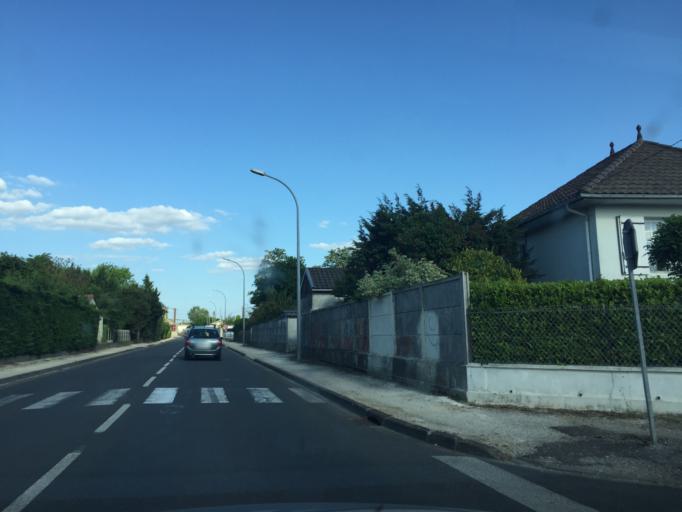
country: FR
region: Aquitaine
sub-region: Departement de la Gironde
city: Coutras
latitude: 45.0362
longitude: -0.1383
